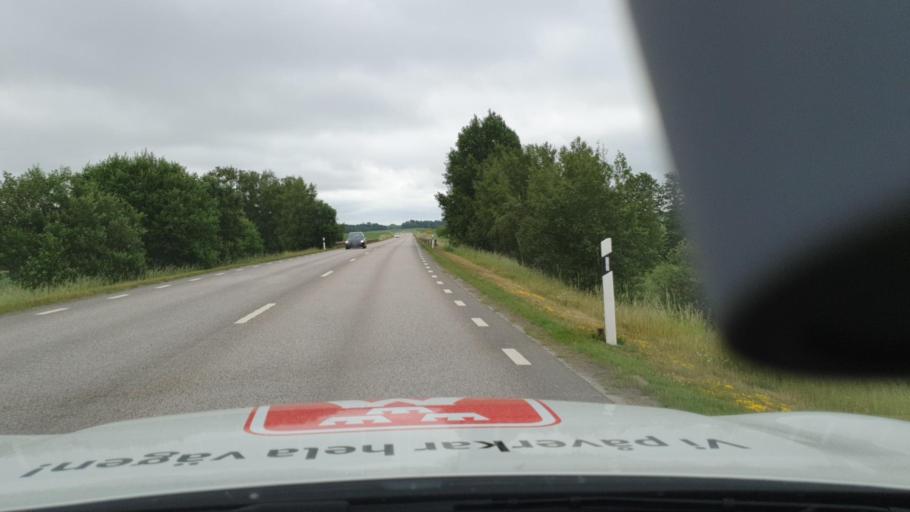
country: SE
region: Vaestra Goetaland
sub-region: Tibro Kommun
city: Tibro
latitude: 58.3513
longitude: 14.0829
